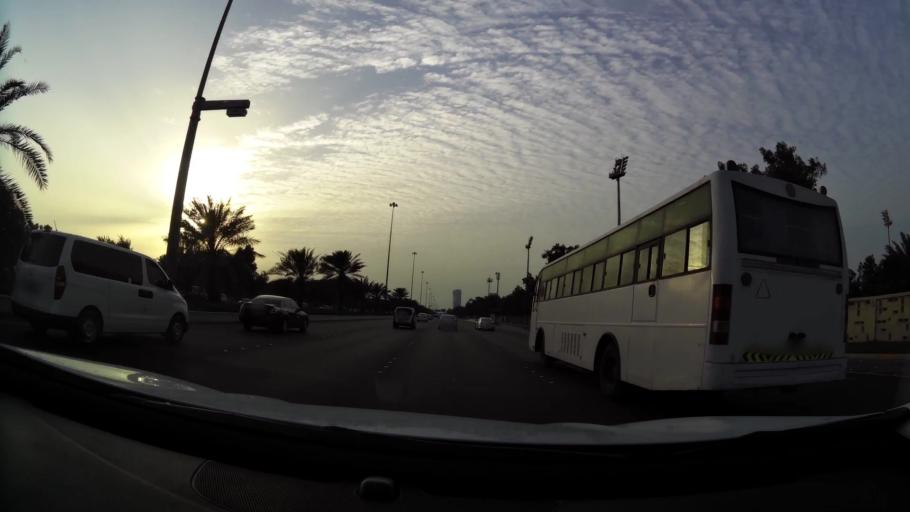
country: AE
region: Abu Dhabi
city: Abu Dhabi
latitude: 24.4107
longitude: 54.4602
